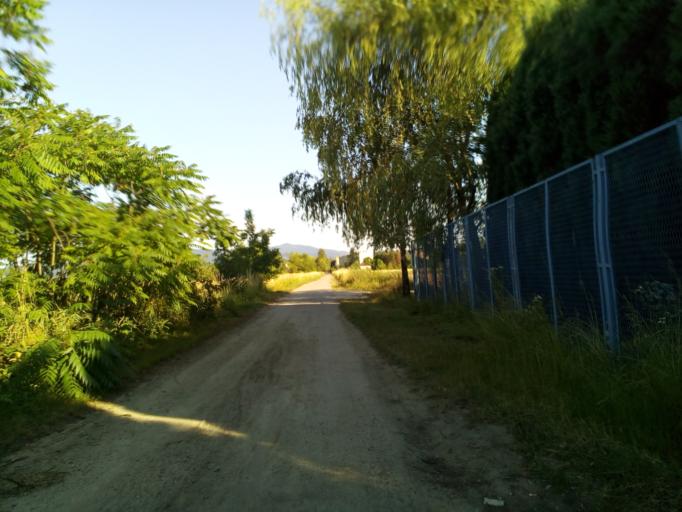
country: PL
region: Lesser Poland Voivodeship
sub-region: Powiat nowosadecki
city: Stary Sacz
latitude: 49.5728
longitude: 20.6239
